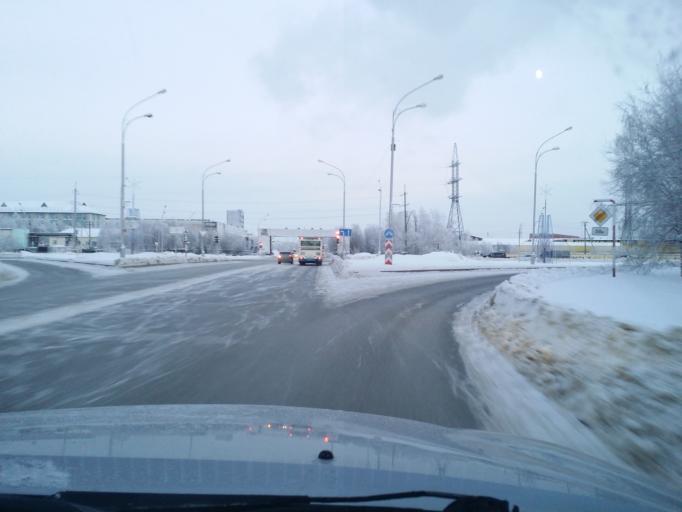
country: RU
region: Khanty-Mansiyskiy Avtonomnyy Okrug
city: Nizhnevartovsk
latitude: 60.9482
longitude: 76.5275
